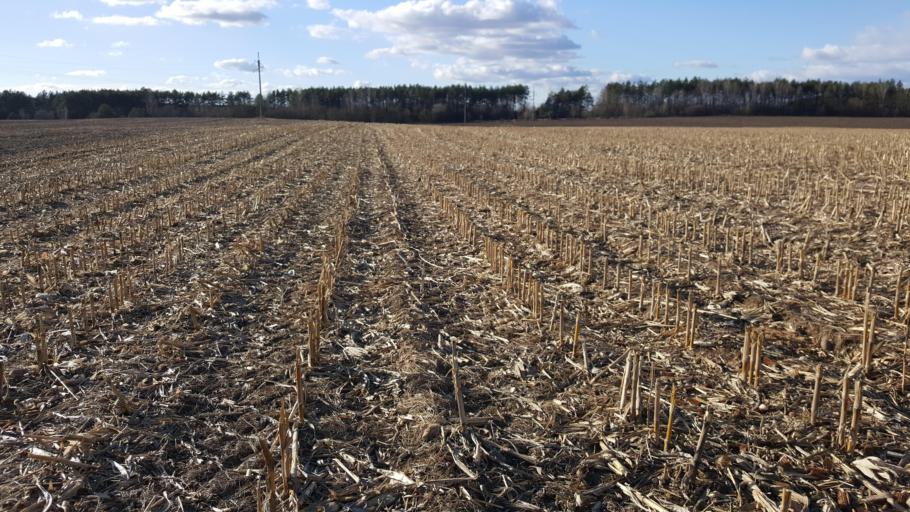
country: BY
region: Brest
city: Kamyanyets
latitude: 52.3830
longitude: 23.8499
